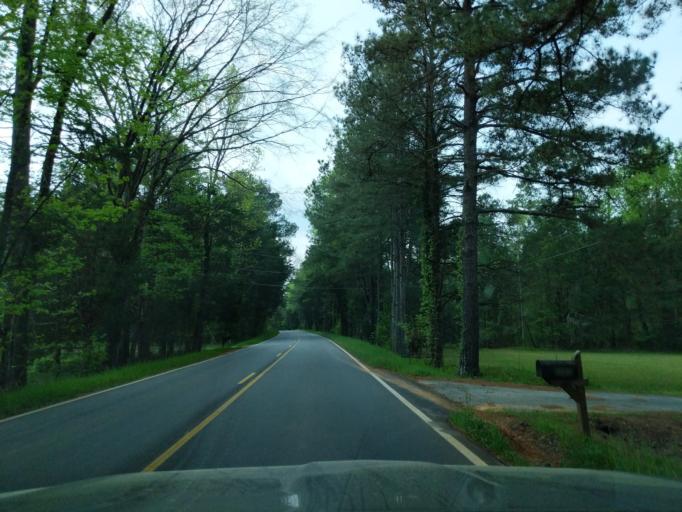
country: US
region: Georgia
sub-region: Columbia County
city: Appling
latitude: 33.6349
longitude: -82.3409
